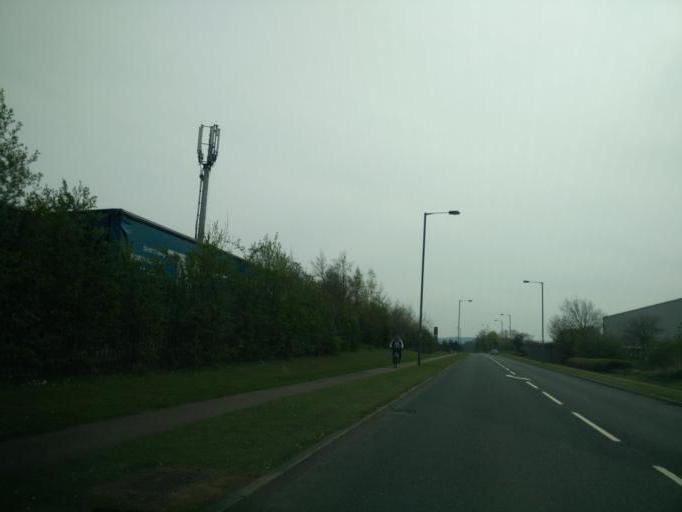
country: GB
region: England
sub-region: County Durham
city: Crook
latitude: 54.7093
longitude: -1.7518
